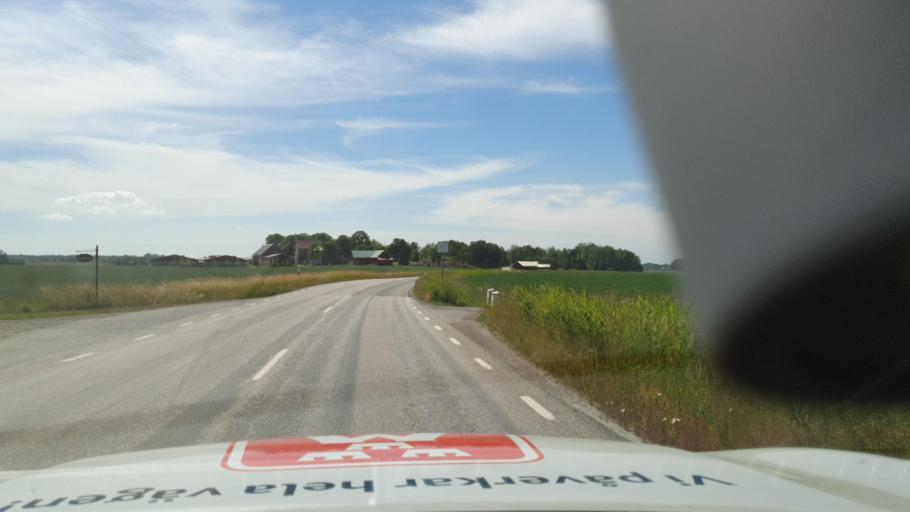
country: SE
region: Vaestra Goetaland
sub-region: Lidkopings Kommun
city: Lidkoping
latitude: 58.5119
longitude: 13.0489
